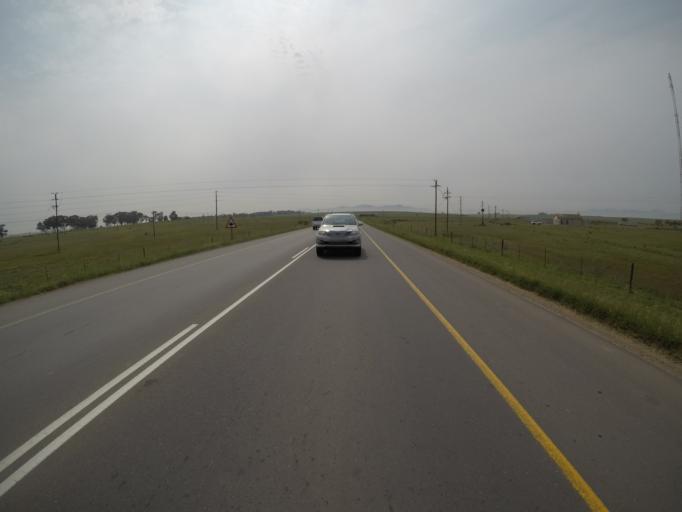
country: ZA
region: Western Cape
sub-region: City of Cape Town
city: Kraaifontein
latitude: -33.7003
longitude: 18.7046
